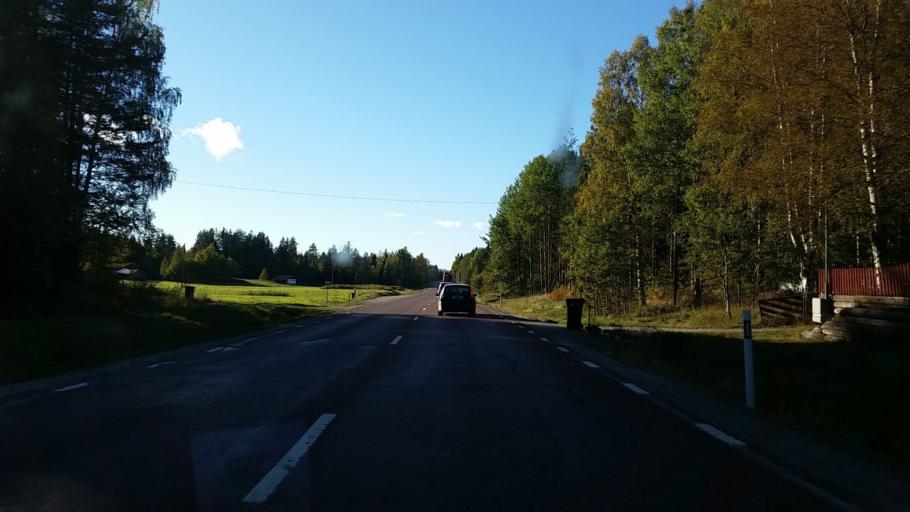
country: SE
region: Gaevleborg
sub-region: Hudiksvalls Kommun
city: Delsbo
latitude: 61.7672
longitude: 16.7065
